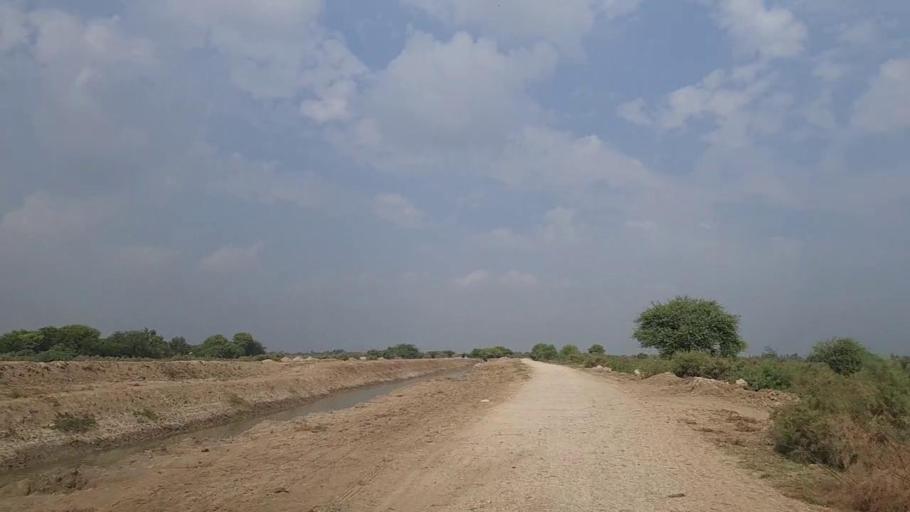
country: PK
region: Sindh
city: Daro Mehar
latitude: 24.6961
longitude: 68.1269
